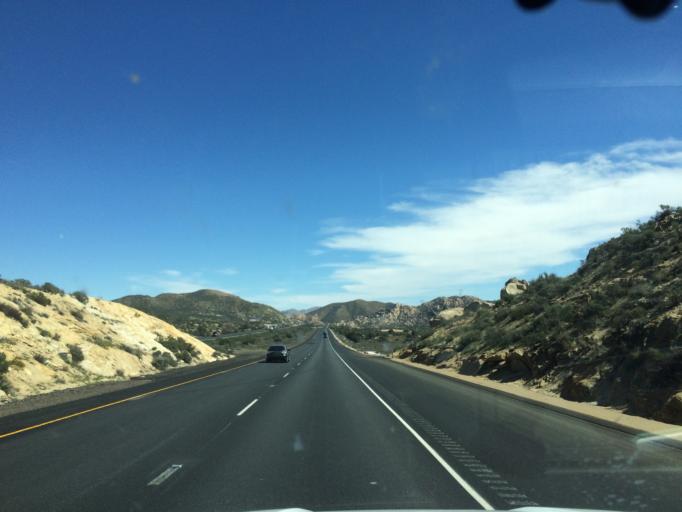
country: MX
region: Baja California
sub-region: Tecate
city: Cereso del Hongo
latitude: 32.6700
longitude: -116.2679
